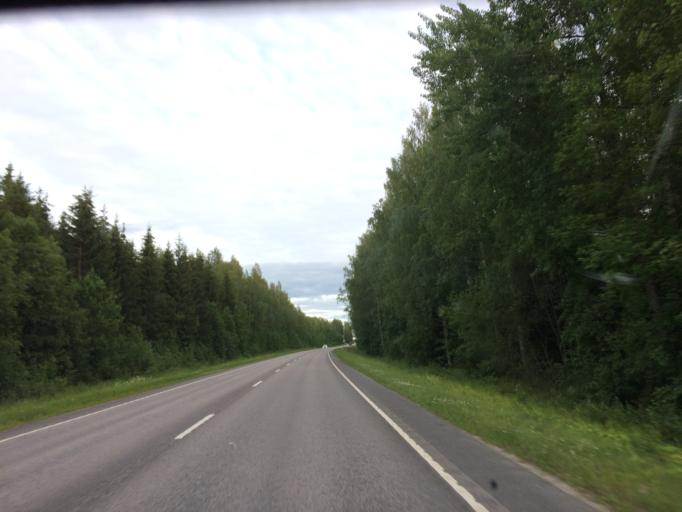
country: FI
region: Haeme
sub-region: Haemeenlinna
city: Tervakoski
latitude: 60.8439
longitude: 24.6139
